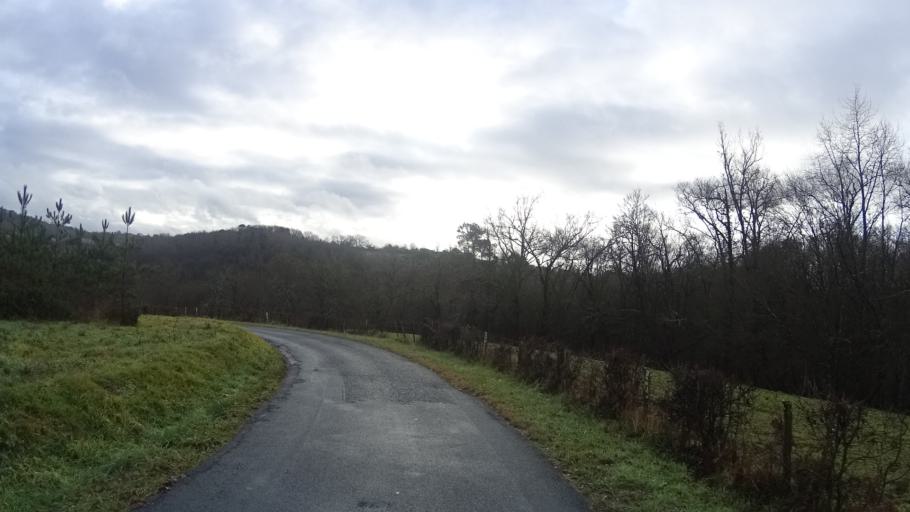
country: FR
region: Aquitaine
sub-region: Departement de la Dordogne
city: Thiviers
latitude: 45.4090
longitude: 0.9697
